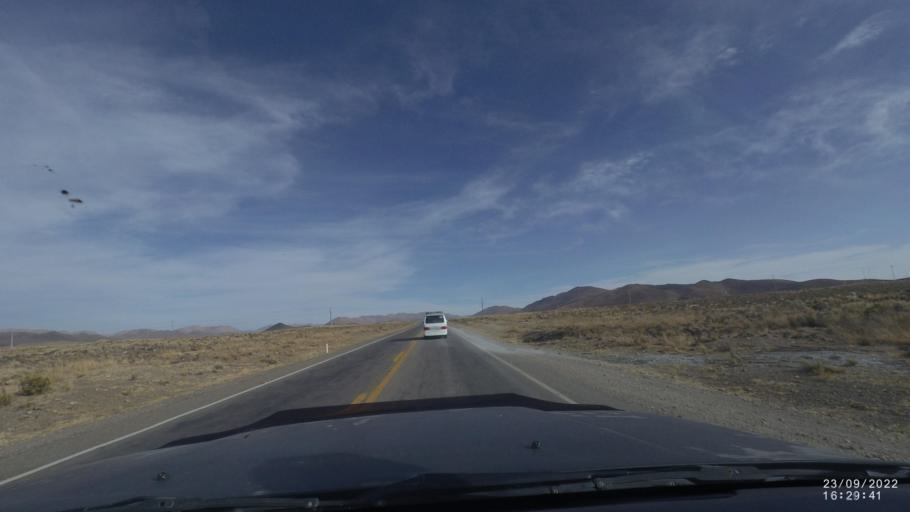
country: BO
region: Oruro
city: Machacamarca
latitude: -18.1459
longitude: -66.9912
